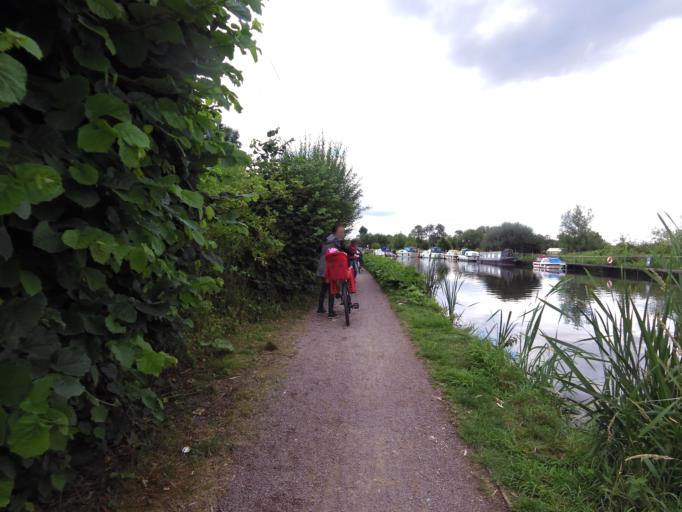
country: GB
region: England
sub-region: Hertfordshire
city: Broxbourne
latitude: 51.7342
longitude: -0.0133
